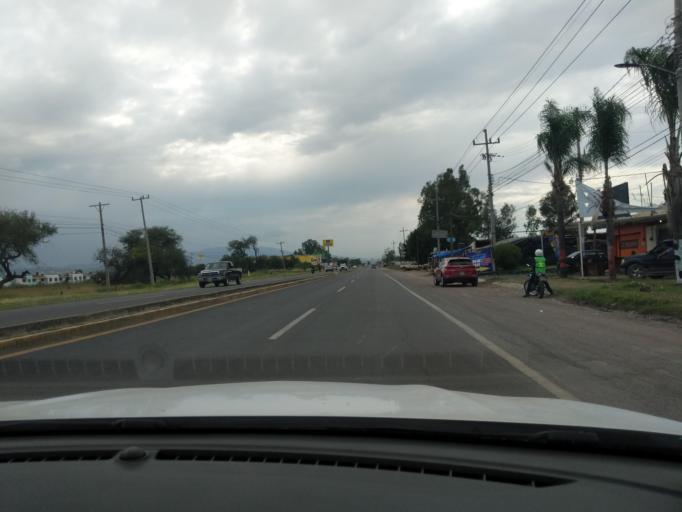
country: MX
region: Jalisco
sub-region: El Salto
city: Galaxia Bonito Jalisco
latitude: 20.5088
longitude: -103.2020
